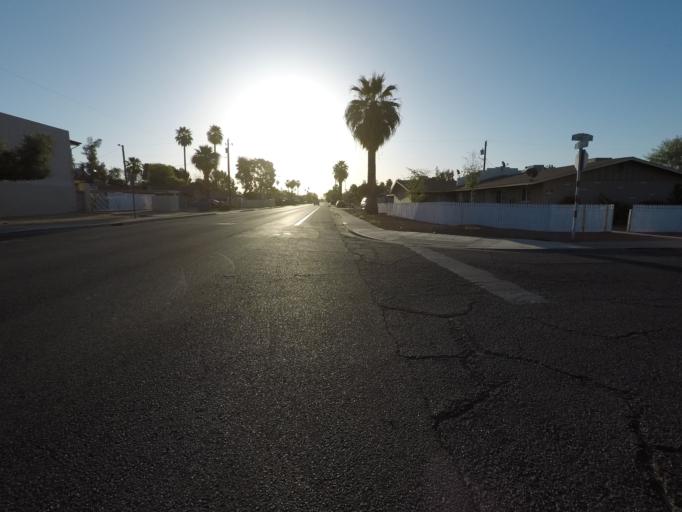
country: US
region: Arizona
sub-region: Maricopa County
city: Phoenix
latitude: 33.4730
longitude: -112.0216
